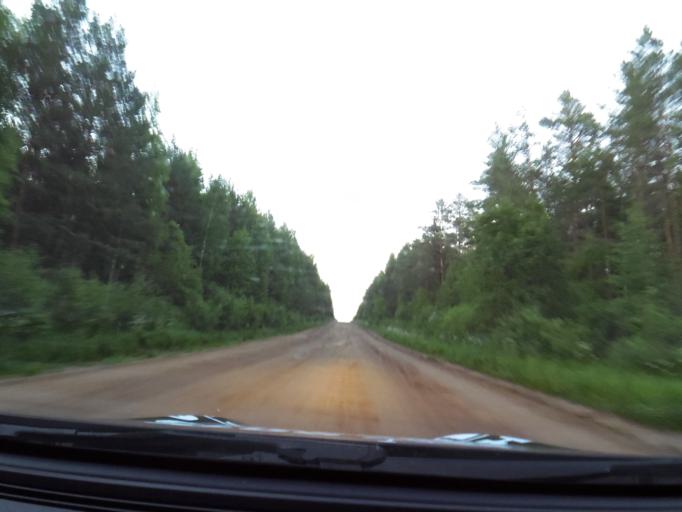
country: RU
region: Leningrad
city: Voznesen'ye
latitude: 60.8602
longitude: 35.9389
